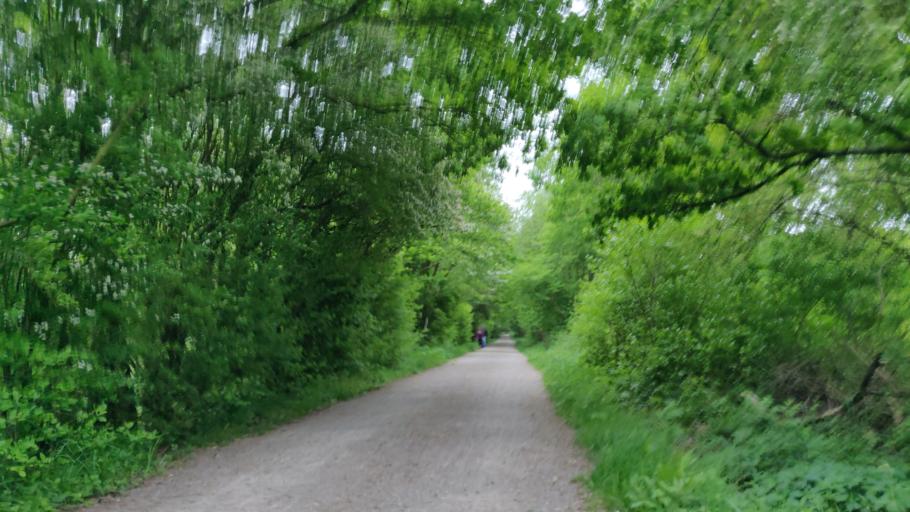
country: GB
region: England
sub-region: West Sussex
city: Southwater
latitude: 51.0088
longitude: -0.3296
